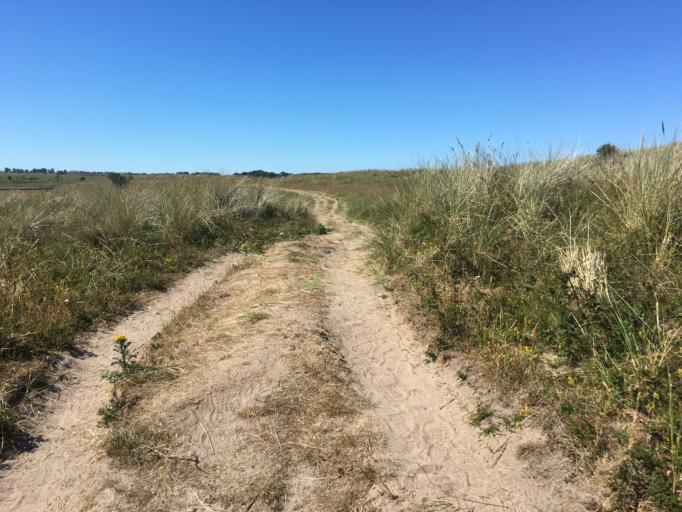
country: GB
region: England
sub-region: Northumberland
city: Beadnell
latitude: 55.5354
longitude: -1.6395
